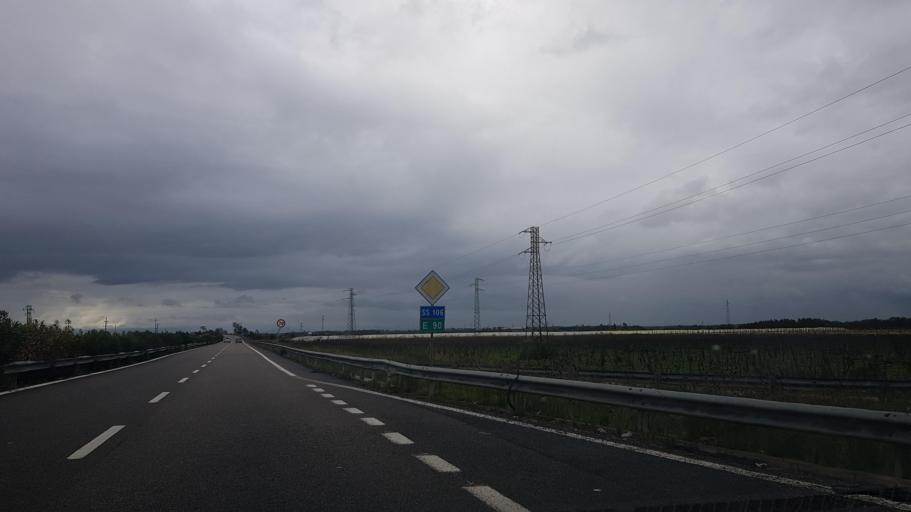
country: IT
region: Apulia
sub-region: Provincia di Taranto
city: Marina di Ginosa
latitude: 40.4328
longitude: 16.8332
